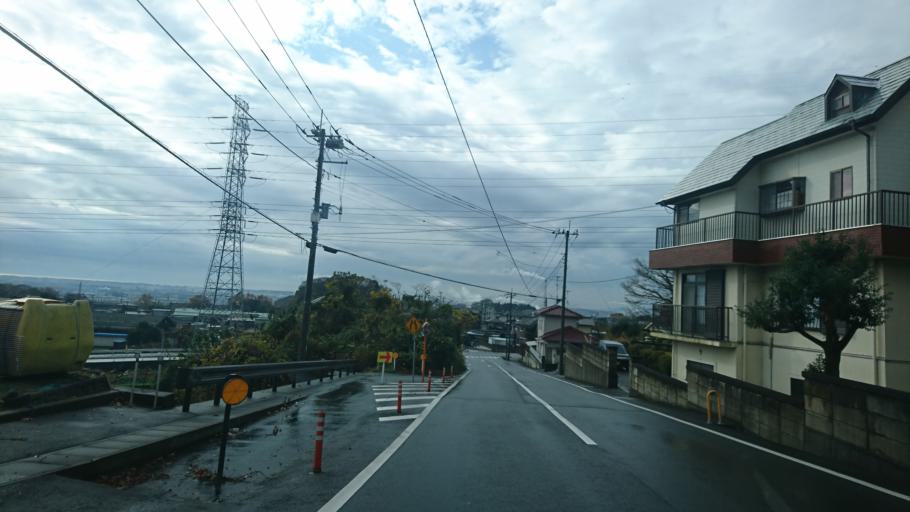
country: JP
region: Shizuoka
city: Fuji
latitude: 35.1739
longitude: 138.7283
